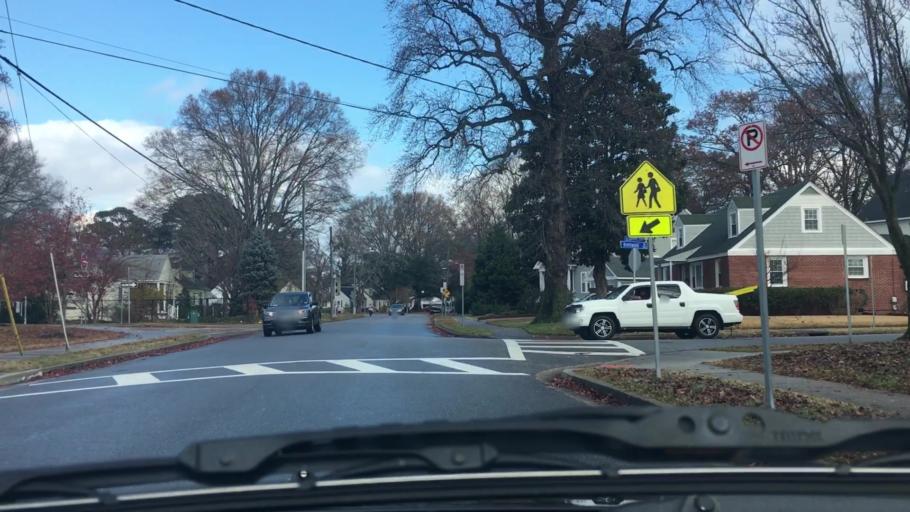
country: US
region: Virginia
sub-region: City of Norfolk
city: Norfolk
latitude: 36.9182
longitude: -76.2504
